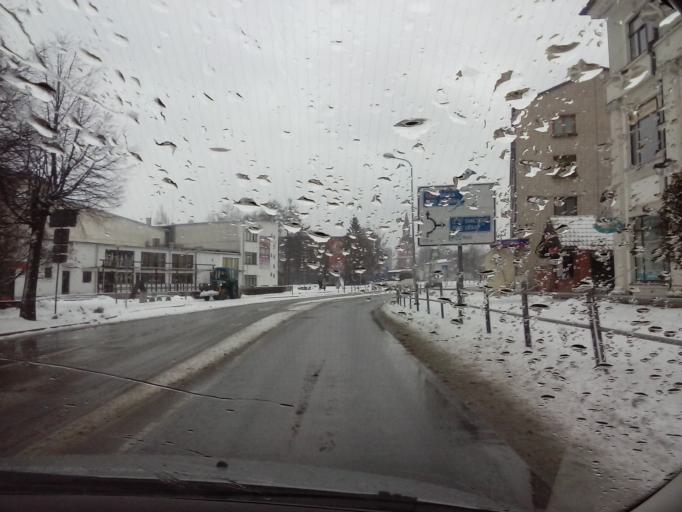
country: LV
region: Valmieras Rajons
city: Valmiera
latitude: 57.5383
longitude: 25.4195
